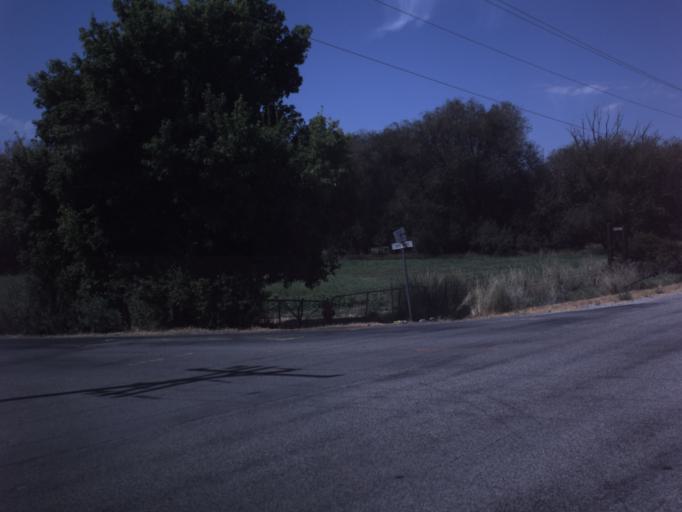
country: US
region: Utah
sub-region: Box Elder County
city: Willard
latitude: 41.4226
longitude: -112.0420
